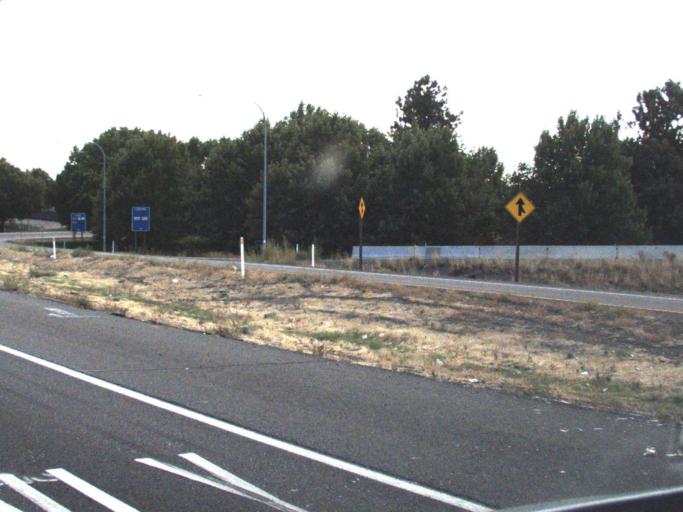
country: US
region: Washington
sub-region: Yakima County
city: Yakima
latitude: 46.6260
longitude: -120.5150
